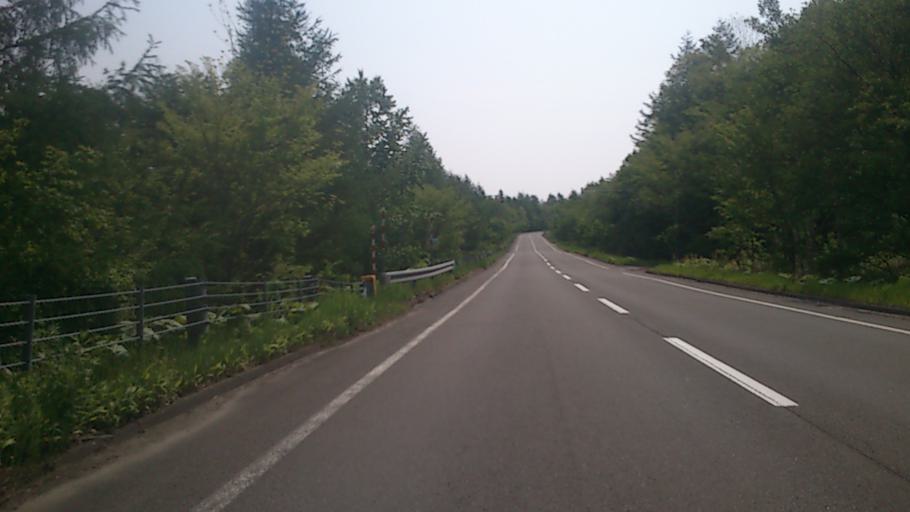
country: JP
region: Hokkaido
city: Bihoro
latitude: 43.4831
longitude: 144.5008
